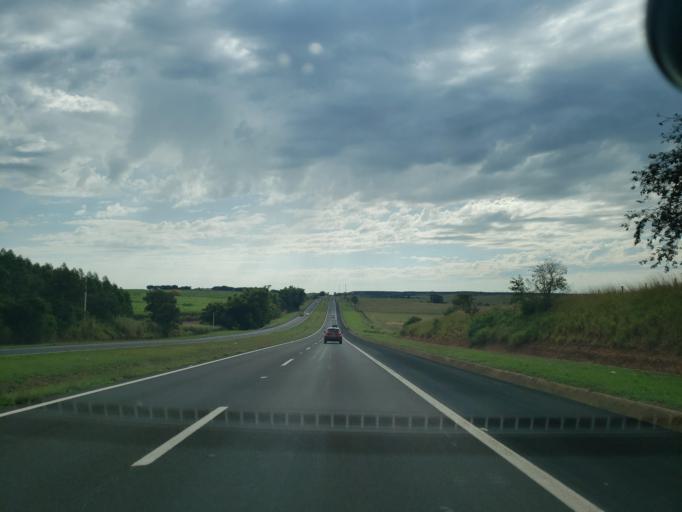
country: BR
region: Sao Paulo
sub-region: Cafelandia
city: Cafelandia
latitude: -21.7855
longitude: -49.6546
